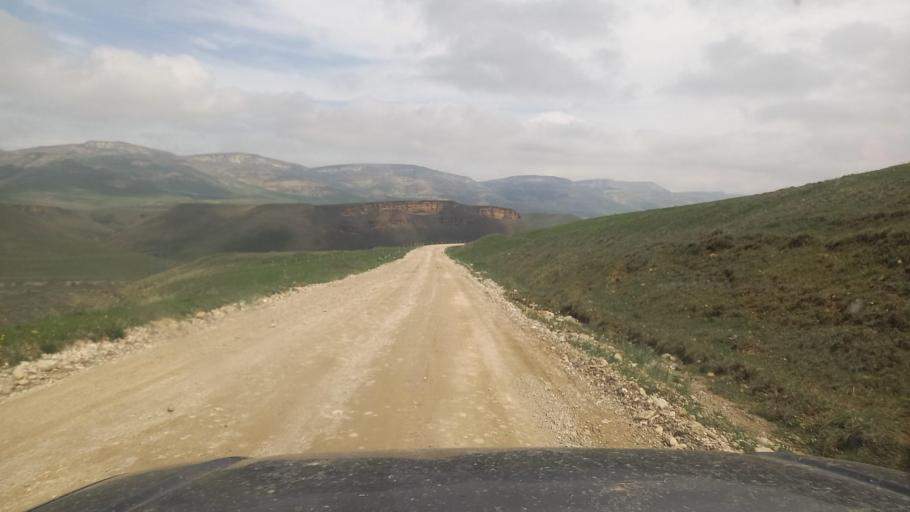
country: RU
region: Stavropol'skiy
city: Kislovodsk
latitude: 43.7984
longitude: 42.8699
